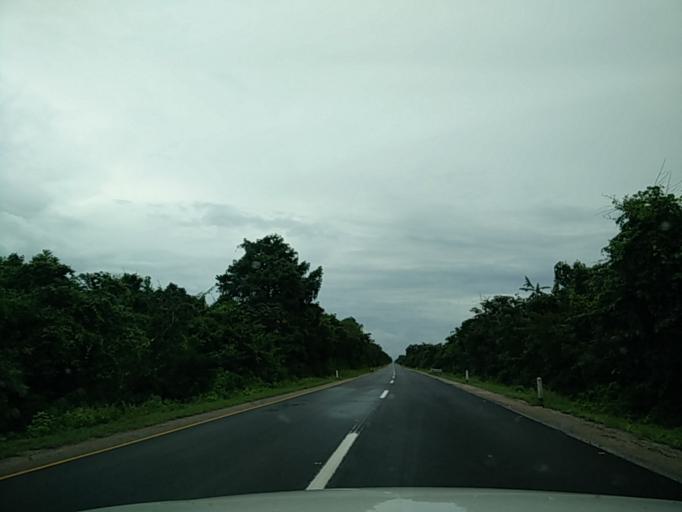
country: MX
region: Quintana Roo
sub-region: Lazaro Cardenas
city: Nuevo Xcan
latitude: 20.8795
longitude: -87.5991
